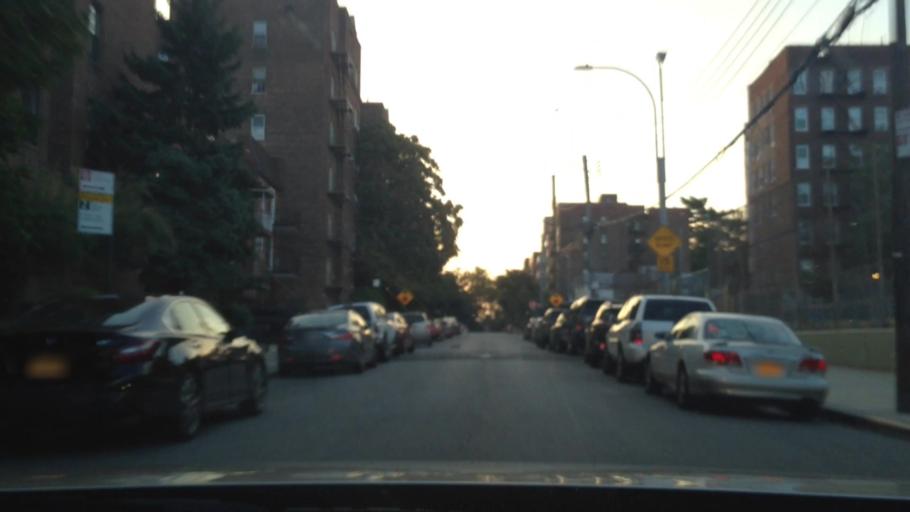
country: US
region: New York
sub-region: Queens County
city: Borough of Queens
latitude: 40.7283
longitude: -73.8624
